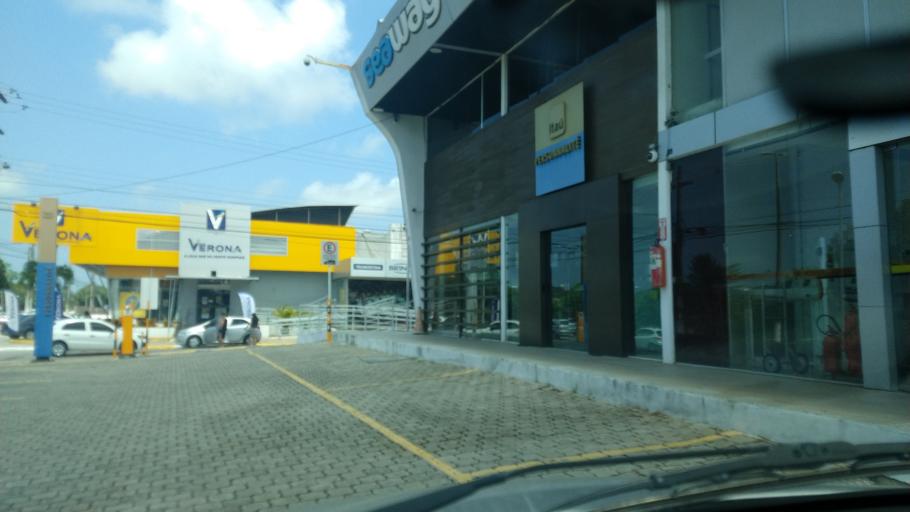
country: BR
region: Rio Grande do Norte
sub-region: Natal
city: Natal
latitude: -5.8599
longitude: -35.1938
